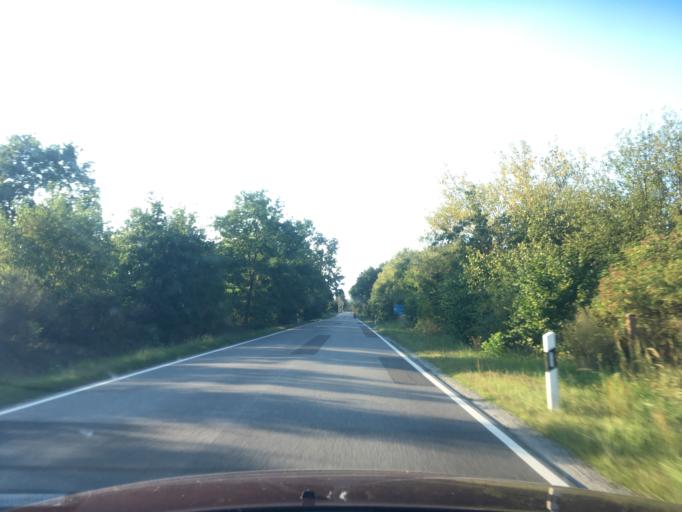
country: DE
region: Saxony
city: Rothenburg
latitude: 51.3242
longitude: 14.9750
